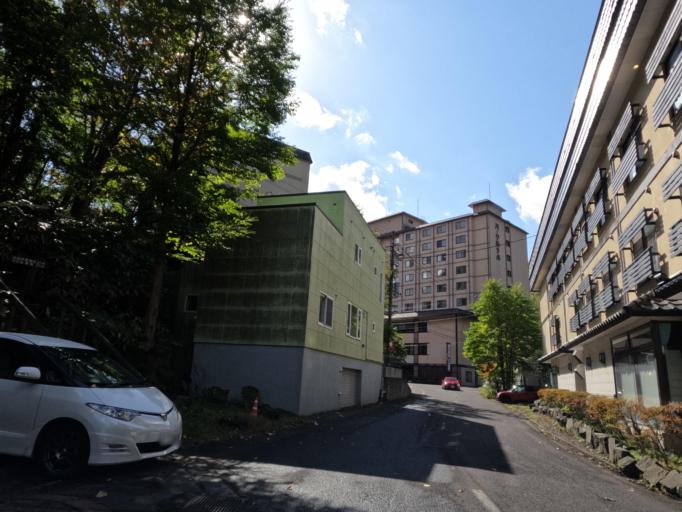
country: JP
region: Hokkaido
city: Shiraoi
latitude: 42.4965
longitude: 141.1415
